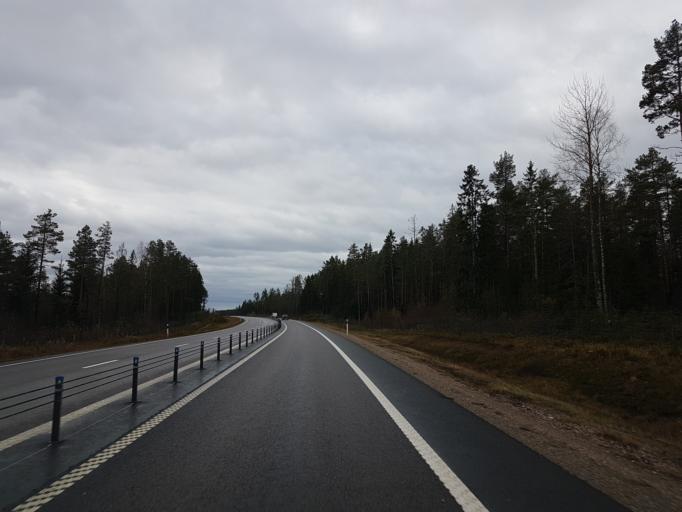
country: SE
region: Vaesternorrland
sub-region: Sundsvalls Kommun
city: Njurundabommen
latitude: 62.1115
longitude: 17.3192
